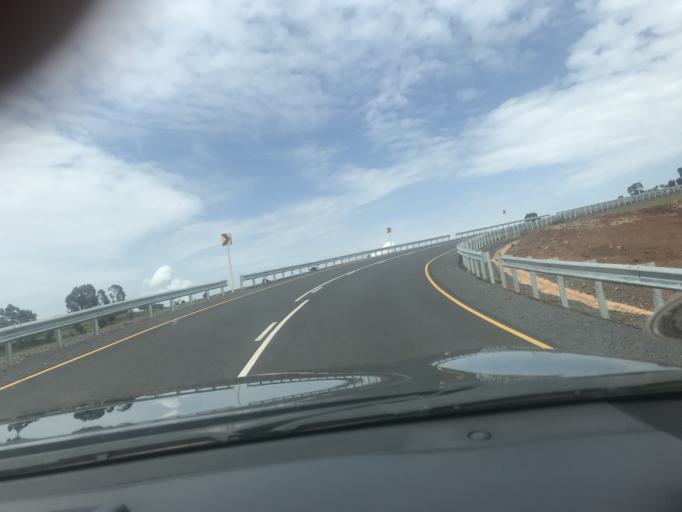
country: ET
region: Oromiya
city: Shambu
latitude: 9.8697
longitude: 36.6934
